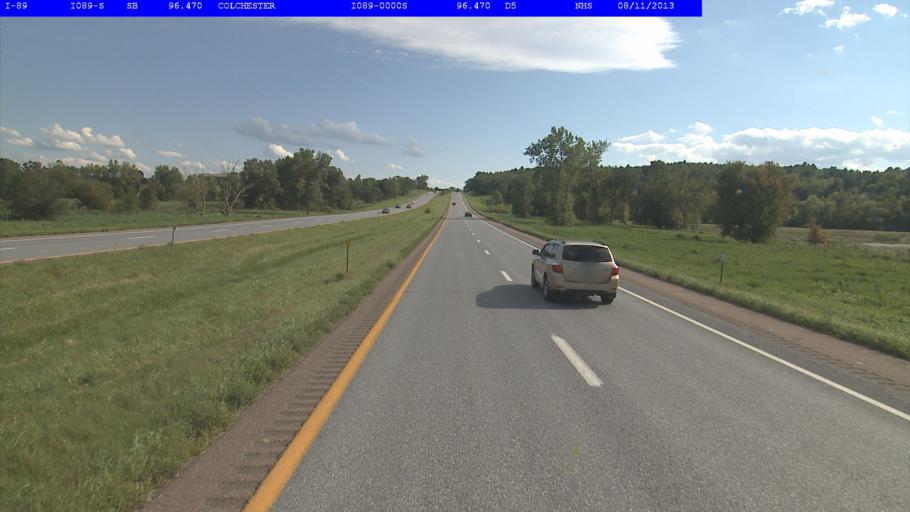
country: US
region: Vermont
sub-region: Chittenden County
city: Colchester
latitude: 44.5705
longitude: -73.1782
